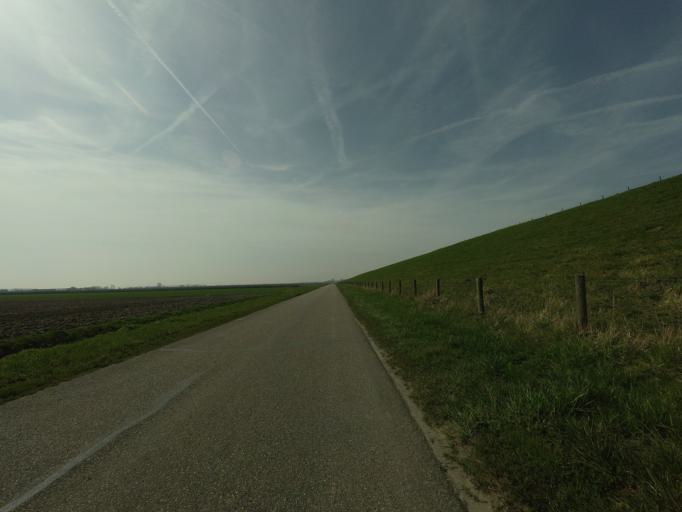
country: NL
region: Zeeland
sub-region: Gemeente Hulst
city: Hulst
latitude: 51.3638
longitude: 4.0793
